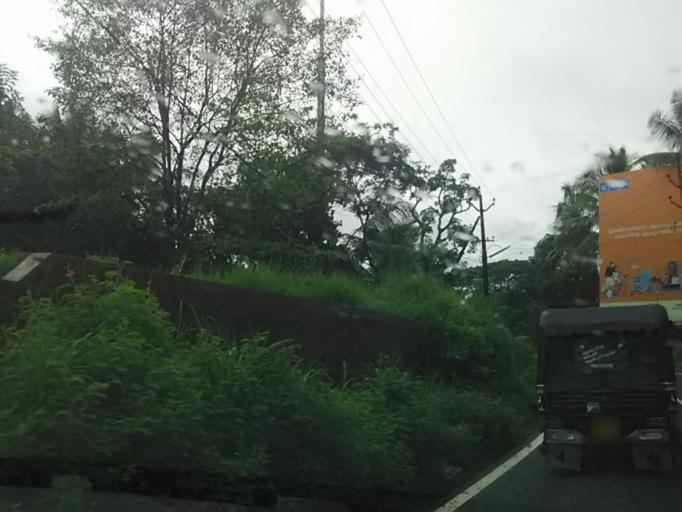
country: IN
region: Kerala
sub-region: Kozhikode
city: Kunnamangalam
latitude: 11.3117
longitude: 75.9155
